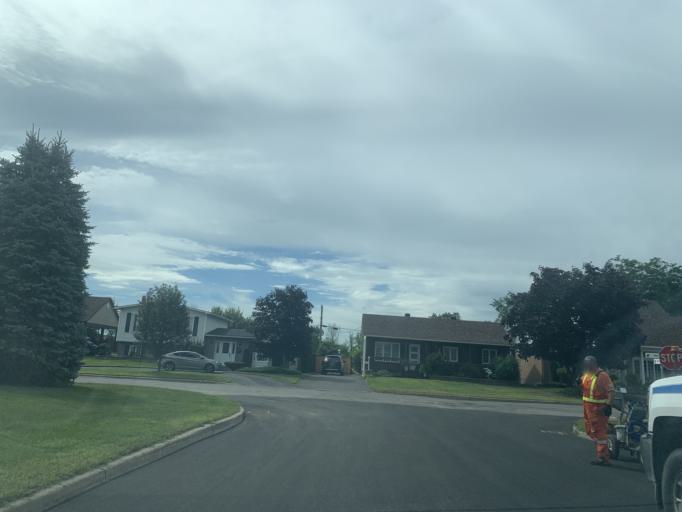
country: CA
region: Ontario
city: Hawkesbury
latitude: 45.6087
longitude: -74.6289
